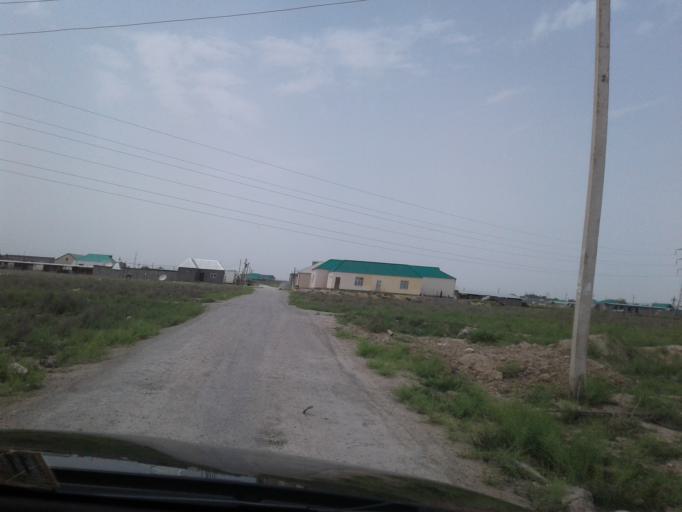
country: TM
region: Ahal
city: Ashgabat
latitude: 37.9810
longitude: 58.3195
